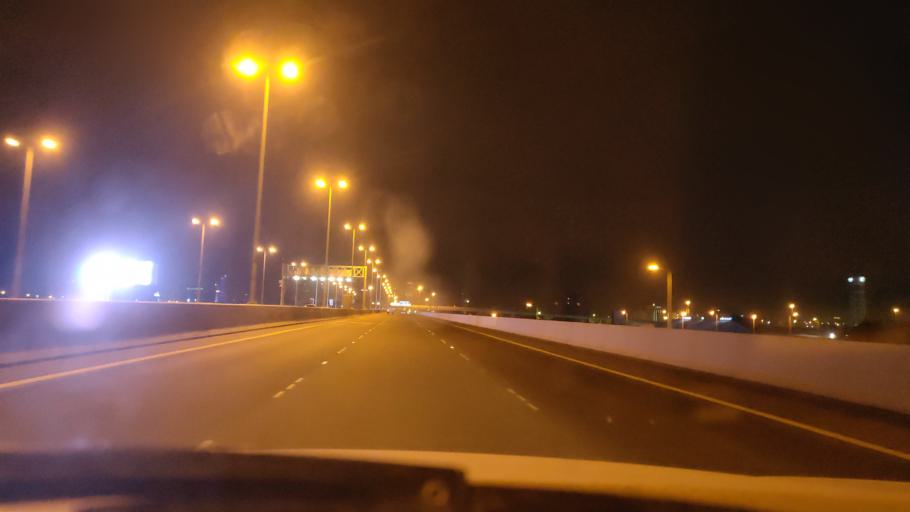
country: KW
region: Al Asimah
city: Ash Shamiyah
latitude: 29.3373
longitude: 47.9398
